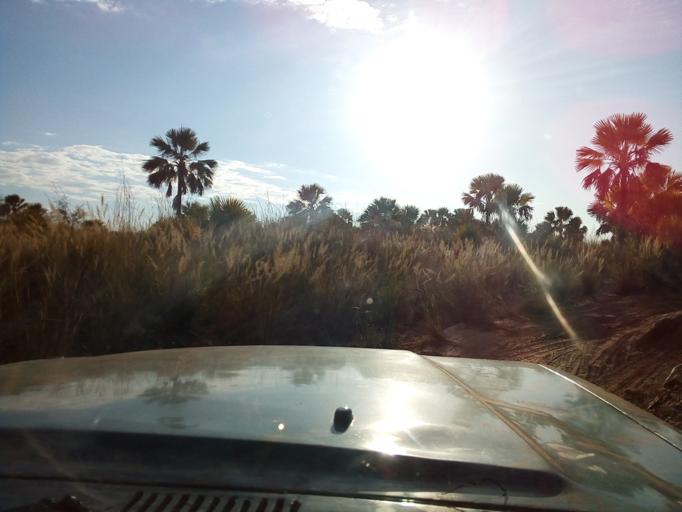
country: MG
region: Boeny
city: Sitampiky
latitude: -16.1244
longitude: 45.5324
